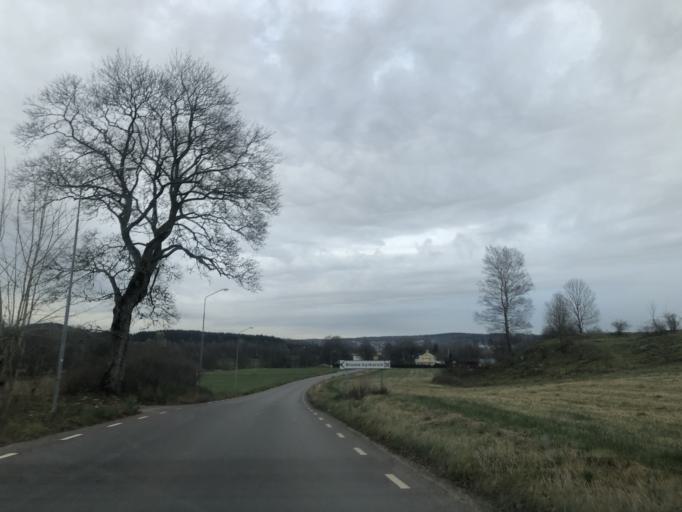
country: SE
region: Vaestra Goetaland
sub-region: Ulricehamns Kommun
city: Ulricehamn
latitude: 57.7981
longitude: 13.3672
